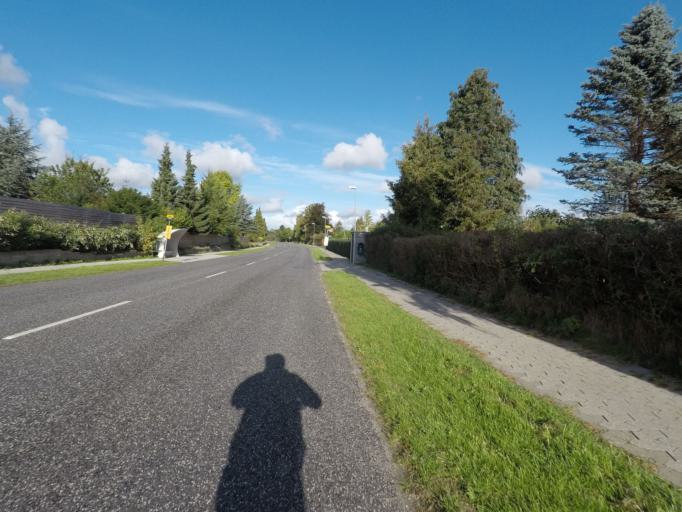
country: DK
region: Capital Region
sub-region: Egedal Kommune
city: Smorumnedre
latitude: 55.7367
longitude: 12.2958
